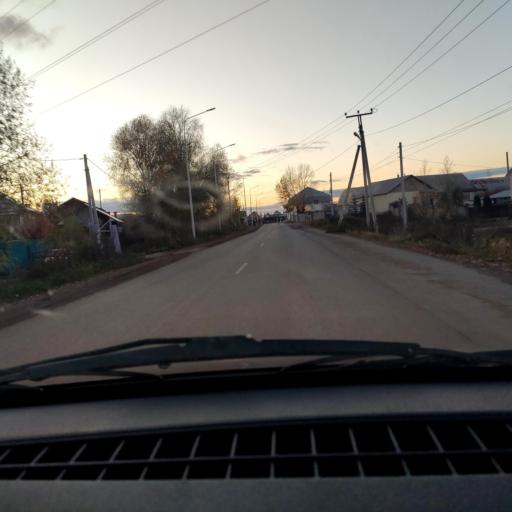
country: RU
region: Bashkortostan
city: Ufa
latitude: 54.6382
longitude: 55.9240
